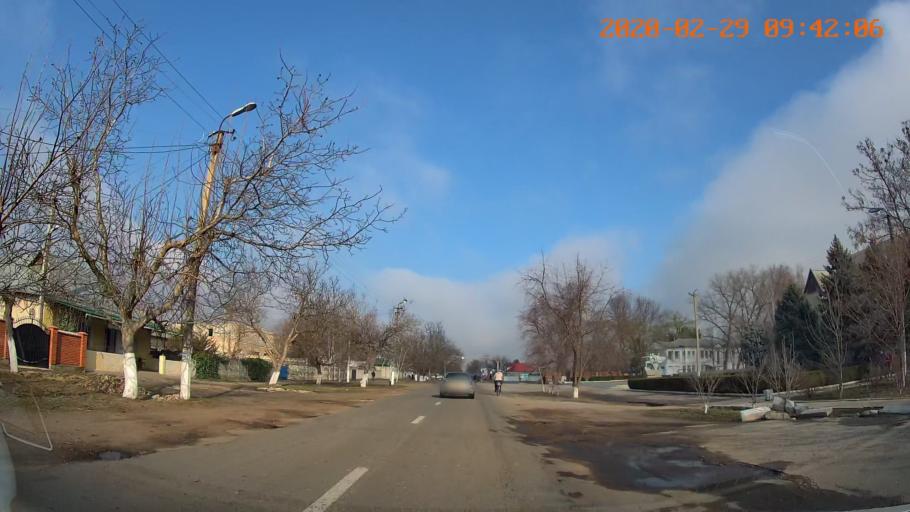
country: MD
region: Telenesti
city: Crasnoe
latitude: 46.6391
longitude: 29.8252
